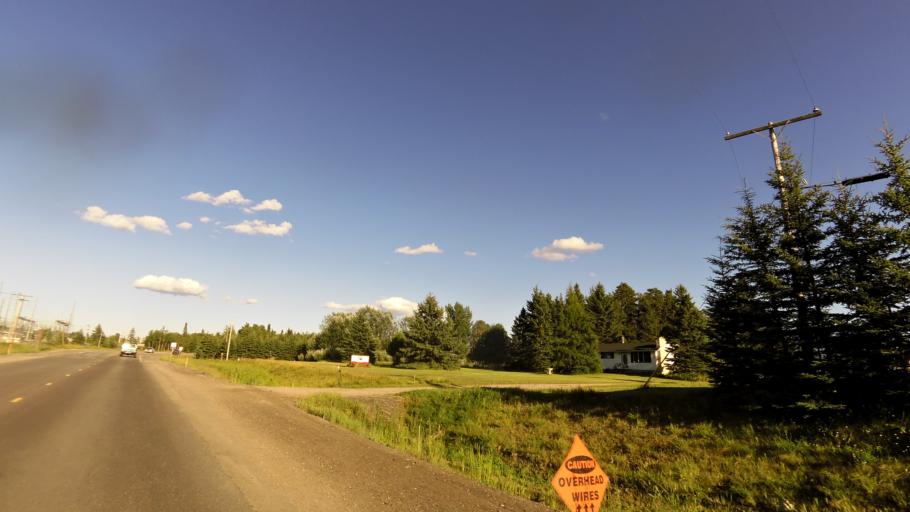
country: CA
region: Ontario
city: Dryden
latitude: 49.8151
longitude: -92.8545
